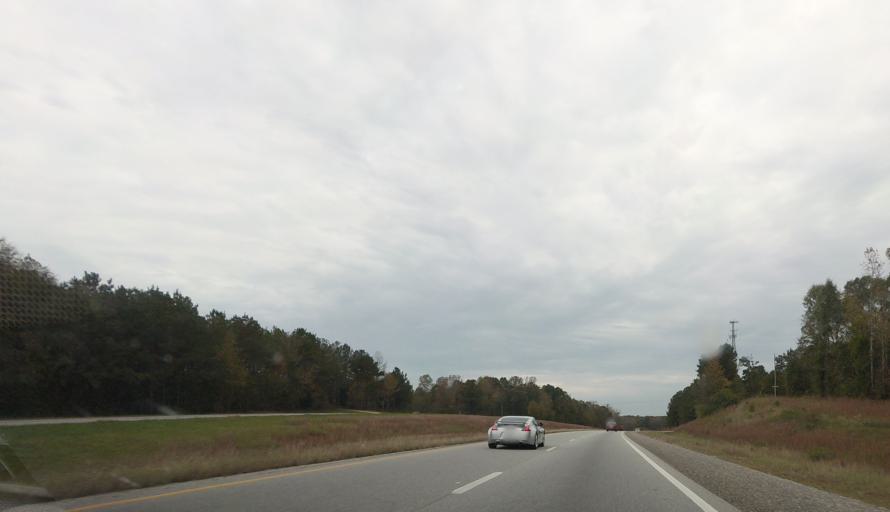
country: US
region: Alabama
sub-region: Lee County
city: Opelika
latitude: 32.6383
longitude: -85.3093
